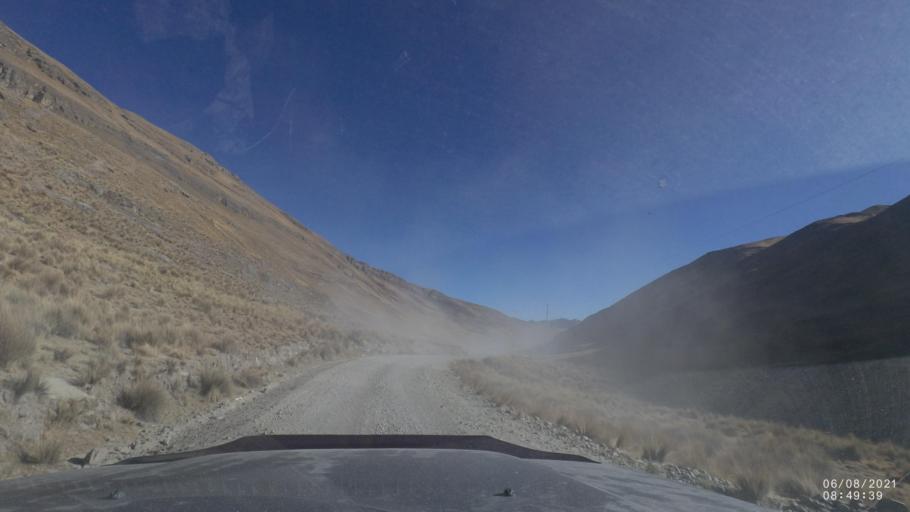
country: BO
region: Cochabamba
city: Sipe Sipe
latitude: -17.1554
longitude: -66.4331
